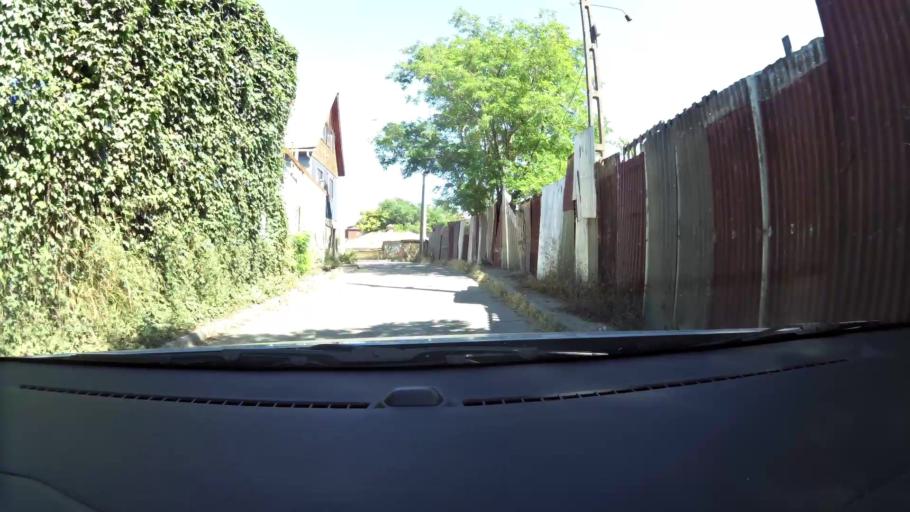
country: CL
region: Valparaiso
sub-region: Provincia de Valparaiso
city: Valparaiso
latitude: -33.0616
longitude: -71.5919
